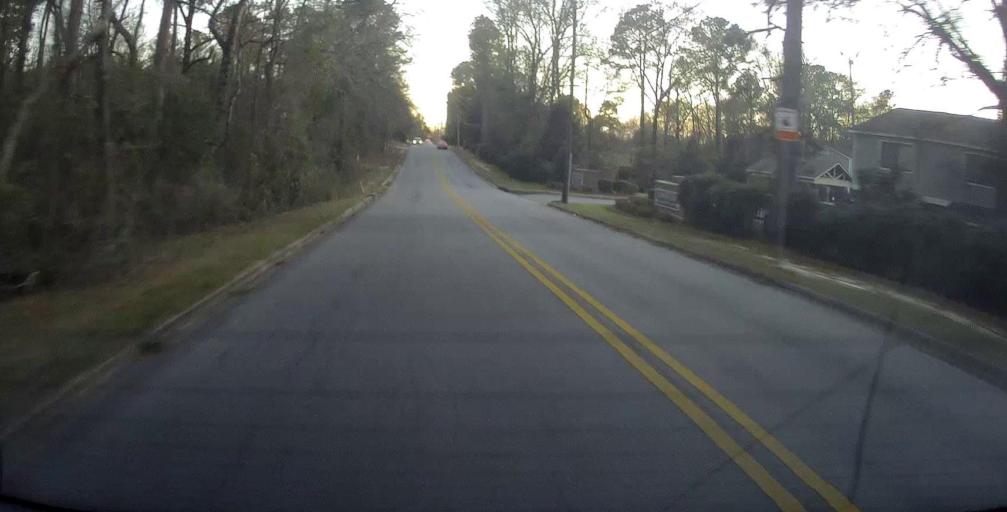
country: US
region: Alabama
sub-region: Russell County
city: Phenix City
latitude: 32.4902
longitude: -85.0193
